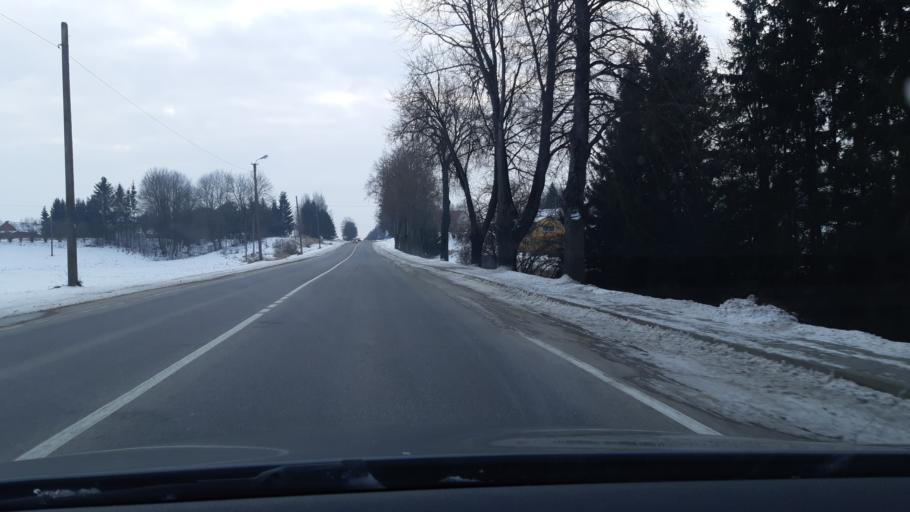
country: LT
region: Kauno apskritis
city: Kedainiai
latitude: 55.2421
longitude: 23.8324
